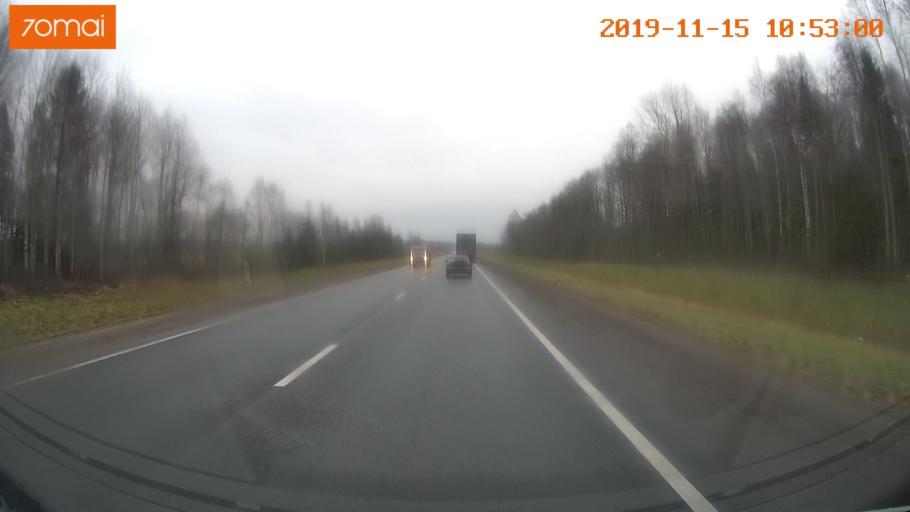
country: RU
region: Vologda
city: Chebsara
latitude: 59.1714
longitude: 38.7447
